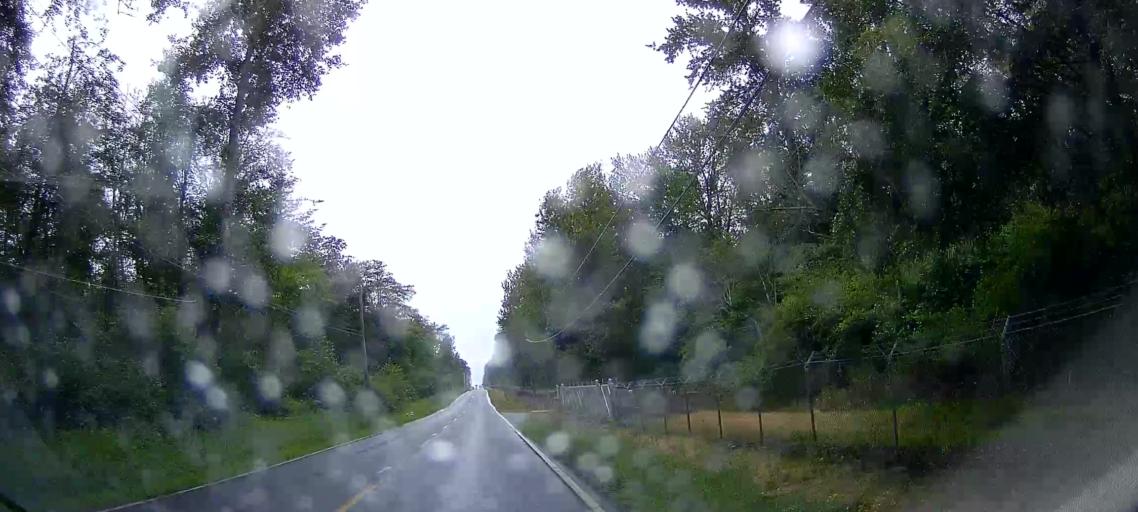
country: US
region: Washington
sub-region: Whatcom County
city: Ferndale
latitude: 48.8196
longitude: -122.6861
